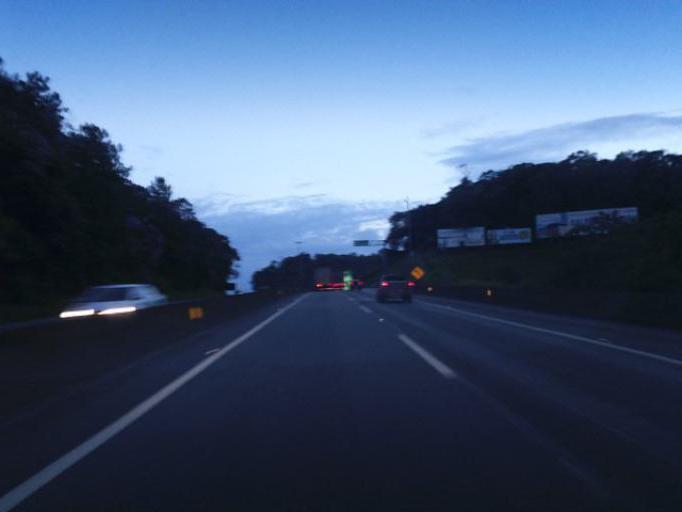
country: BR
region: Santa Catarina
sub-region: Joinville
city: Joinville
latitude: -26.3834
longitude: -48.8507
